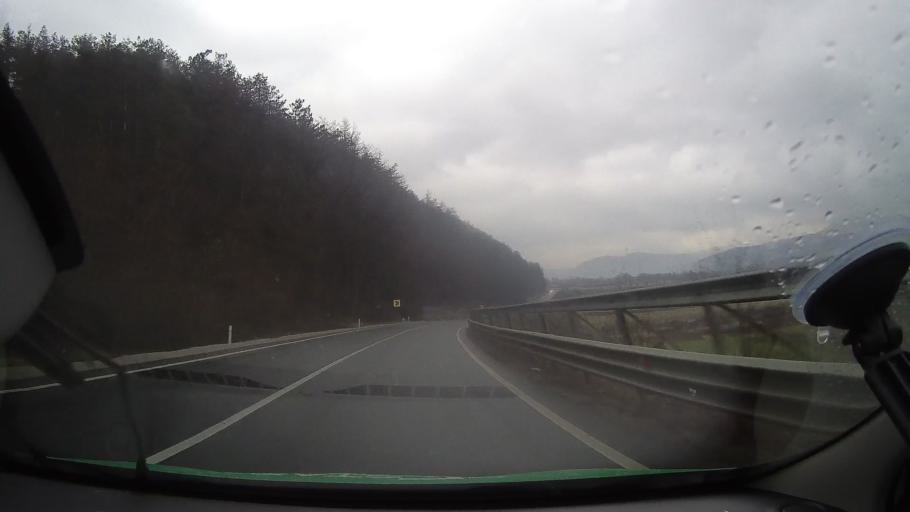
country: RO
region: Hunedoara
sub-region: Comuna Tomesti
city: Tomesti
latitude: 46.1846
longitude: 22.6403
